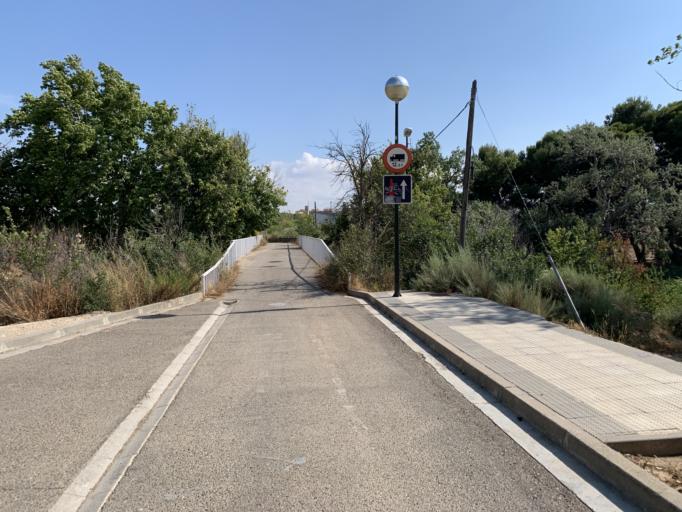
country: ES
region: Aragon
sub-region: Provincia de Zaragoza
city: Oliver-Valdefierro, Oliver, Valdefierro
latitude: 41.6352
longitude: -0.9261
